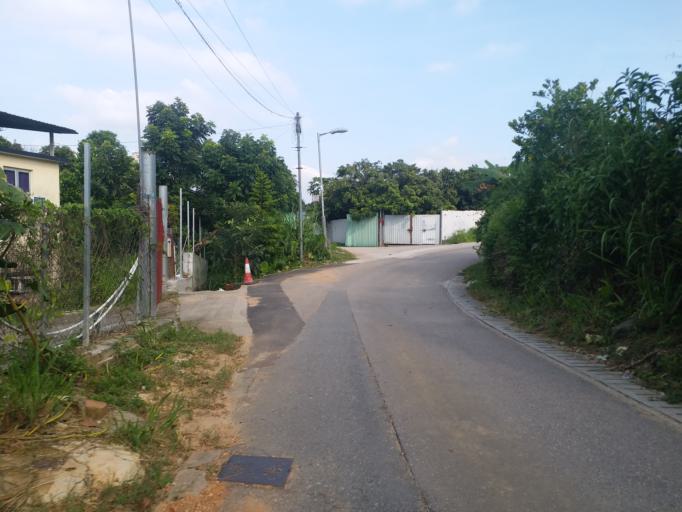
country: HK
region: Yuen Long
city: Yuen Long Kau Hui
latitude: 22.4468
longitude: 114.0118
